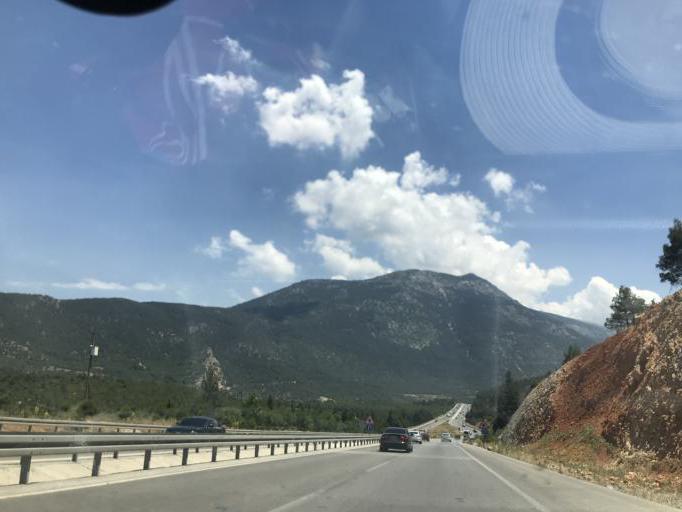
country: TR
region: Denizli
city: Honaz
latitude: 37.7300
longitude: 29.1932
